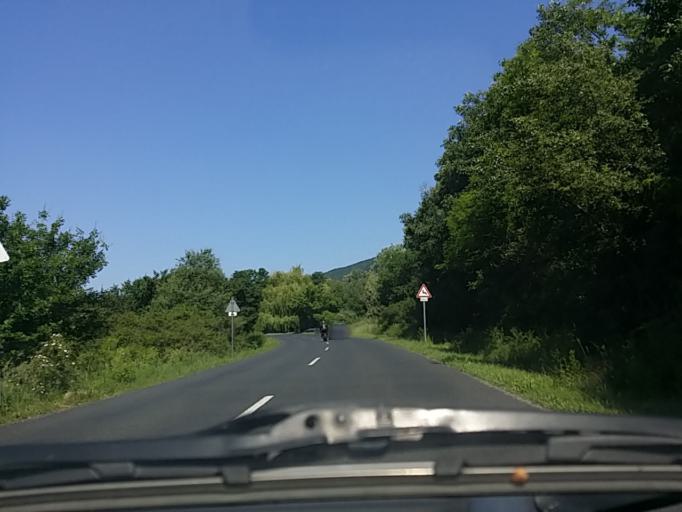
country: HU
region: Pest
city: Pilisszentkereszt
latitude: 47.6793
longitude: 18.9415
